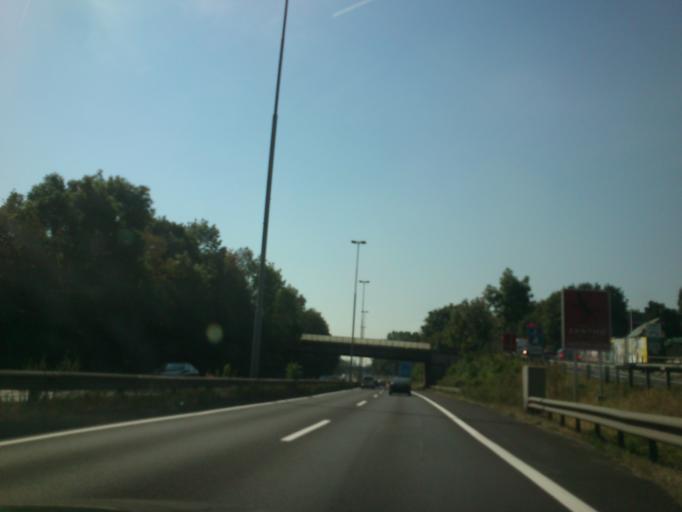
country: AT
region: Upper Austria
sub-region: Linz Stadt
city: Linz
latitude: 48.3024
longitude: 14.3144
